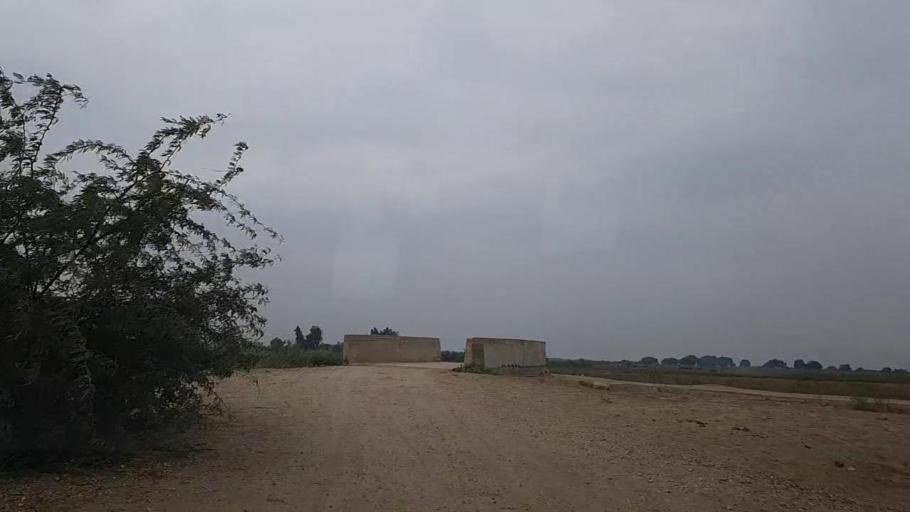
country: PK
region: Sindh
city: Mirpur Sakro
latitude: 24.6152
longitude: 67.7175
